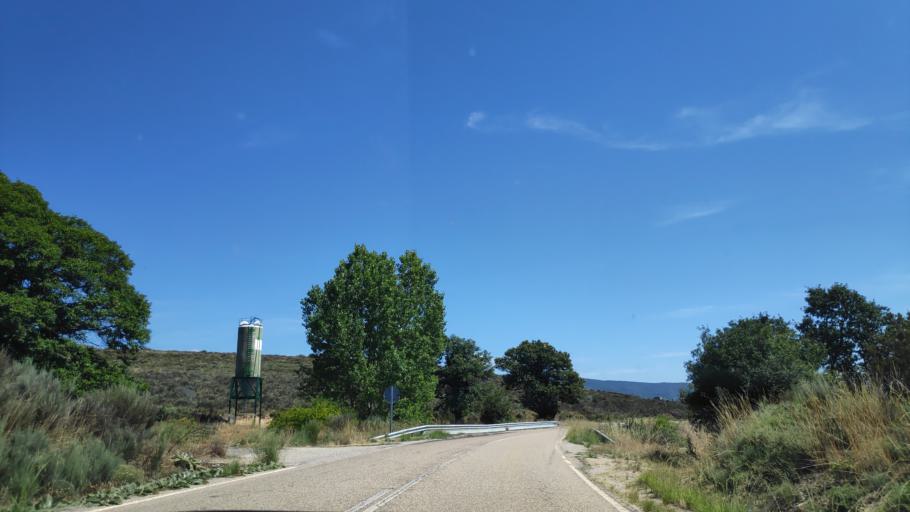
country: ES
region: Castille and Leon
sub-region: Provincia de Zamora
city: Puebla de Sanabria
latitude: 42.0479
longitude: -6.6461
